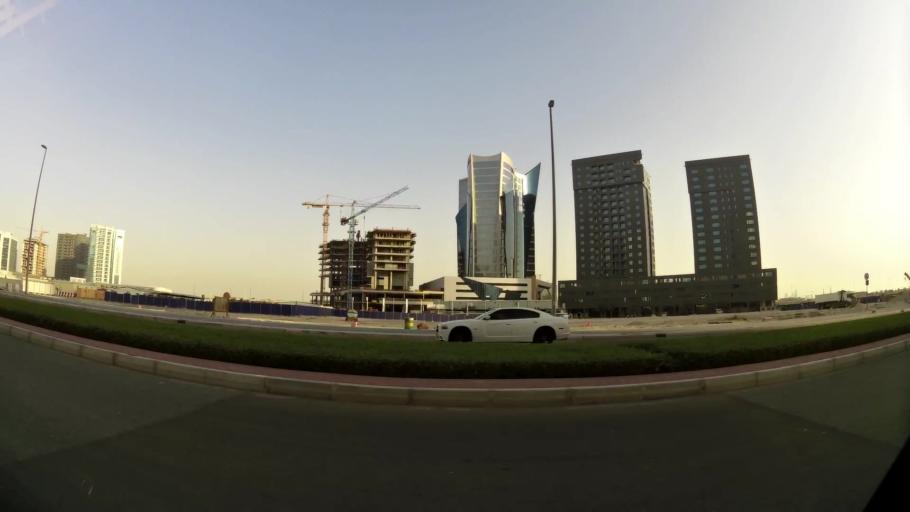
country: AE
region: Dubai
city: Dubai
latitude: 25.1803
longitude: 55.2675
